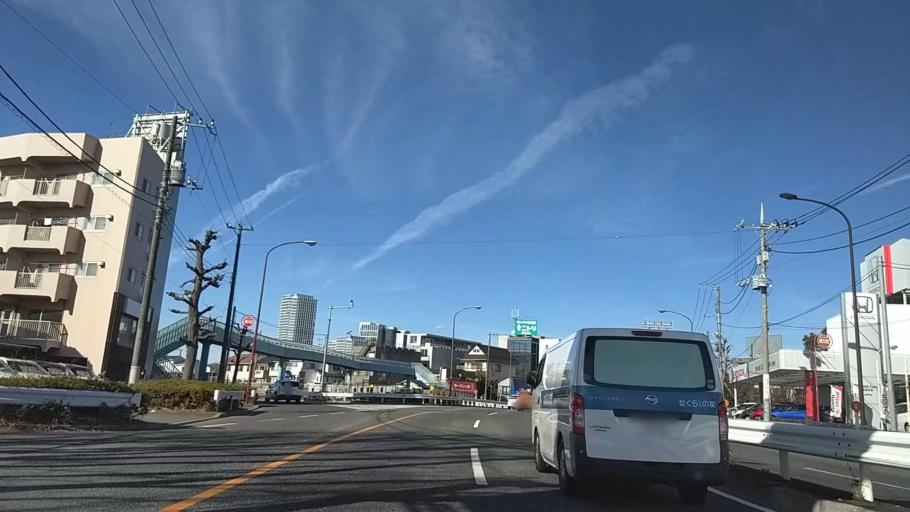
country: JP
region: Tokyo
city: Tokyo
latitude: 35.6067
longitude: 139.6415
